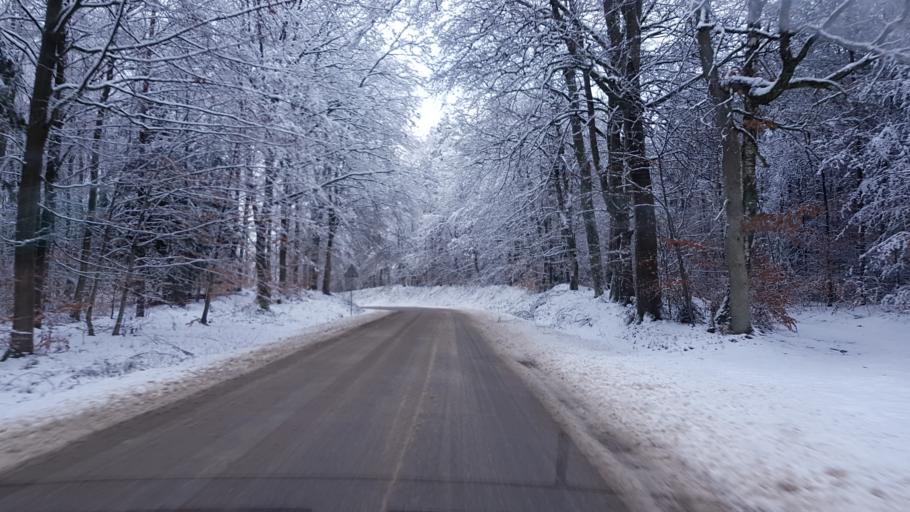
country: PL
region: West Pomeranian Voivodeship
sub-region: Powiat drawski
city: Zlocieniec
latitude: 53.5015
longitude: 15.9966
